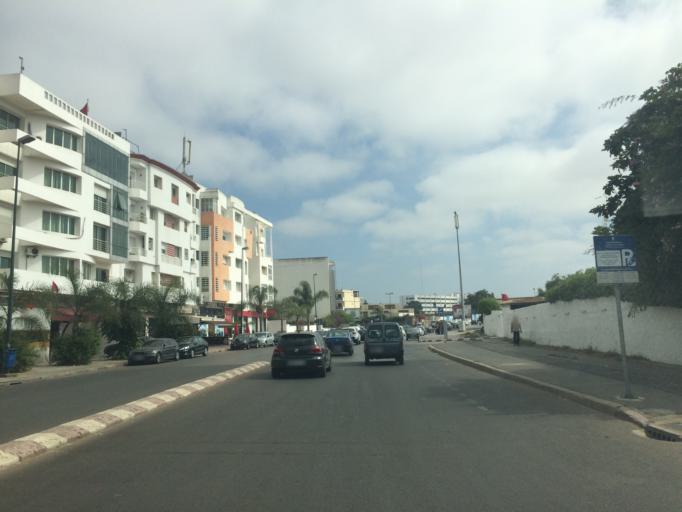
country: MA
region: Rabat-Sale-Zemmour-Zaer
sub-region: Rabat
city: Rabat
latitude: 34.0087
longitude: -6.8517
